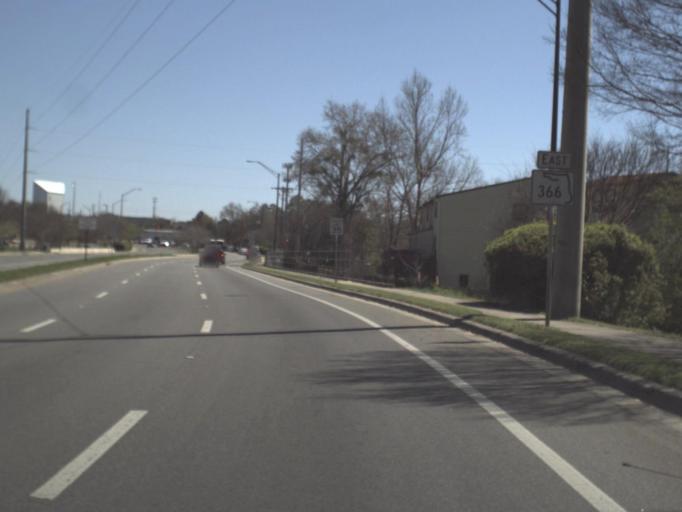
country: US
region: Florida
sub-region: Leon County
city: Tallahassee
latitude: 30.4361
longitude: -84.3054
